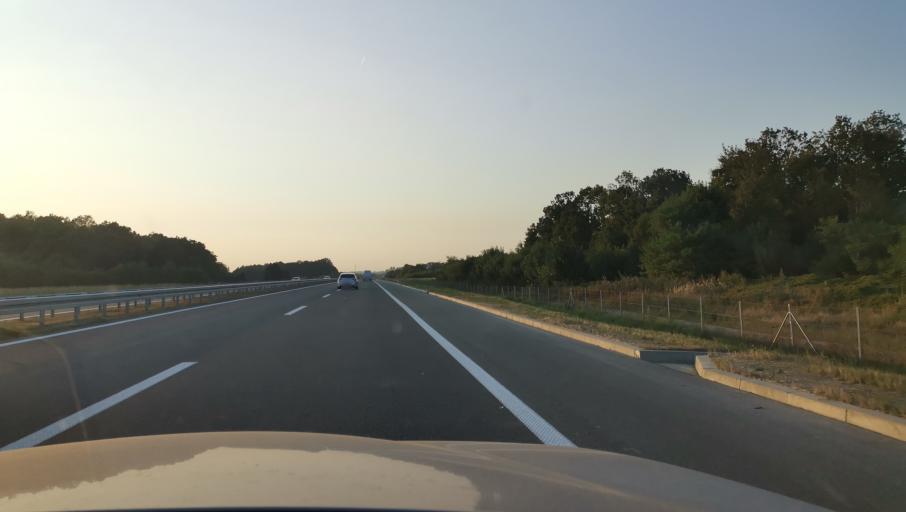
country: RS
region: Central Serbia
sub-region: Kolubarski Okrug
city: Lajkovac
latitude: 44.3867
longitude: 20.1080
